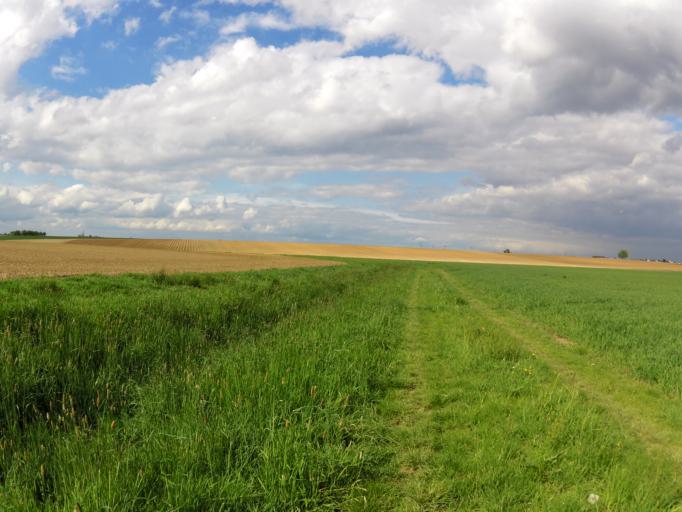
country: DE
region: Bavaria
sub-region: Regierungsbezirk Unterfranken
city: Oberpleichfeld
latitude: 49.8628
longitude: 10.0722
